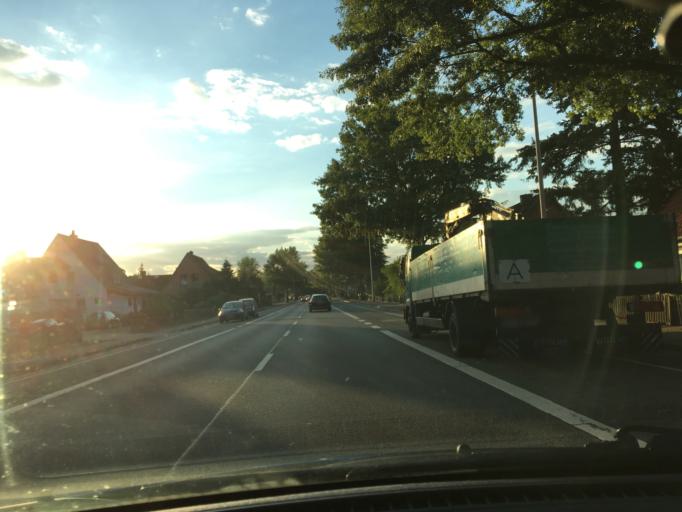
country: DE
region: Lower Saxony
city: Celle
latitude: 52.6554
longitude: 10.0598
